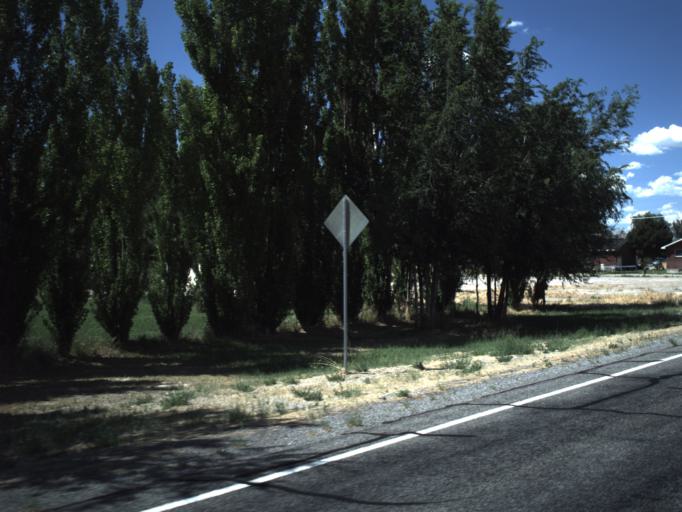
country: US
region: Utah
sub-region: Millard County
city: Delta
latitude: 39.5184
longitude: -112.3720
